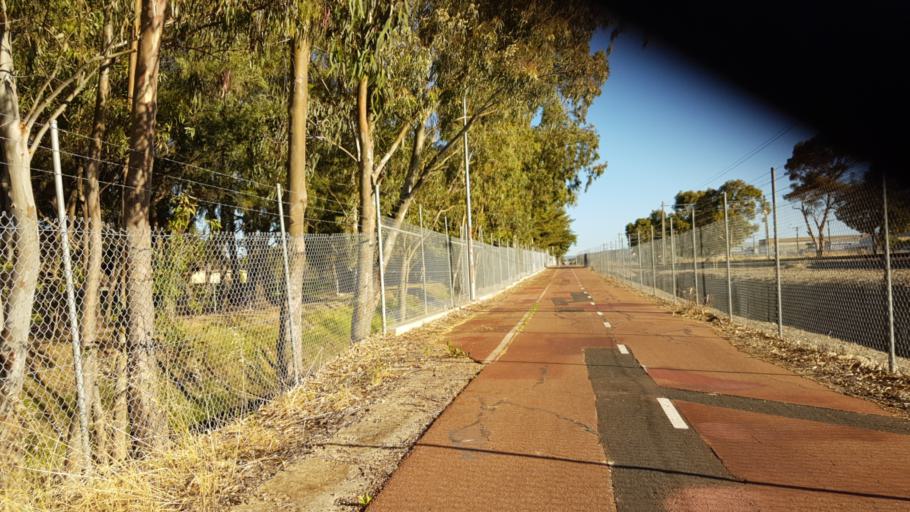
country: AU
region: Western Australia
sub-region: Gosnells
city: Kenwick
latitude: -32.0420
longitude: 115.9746
